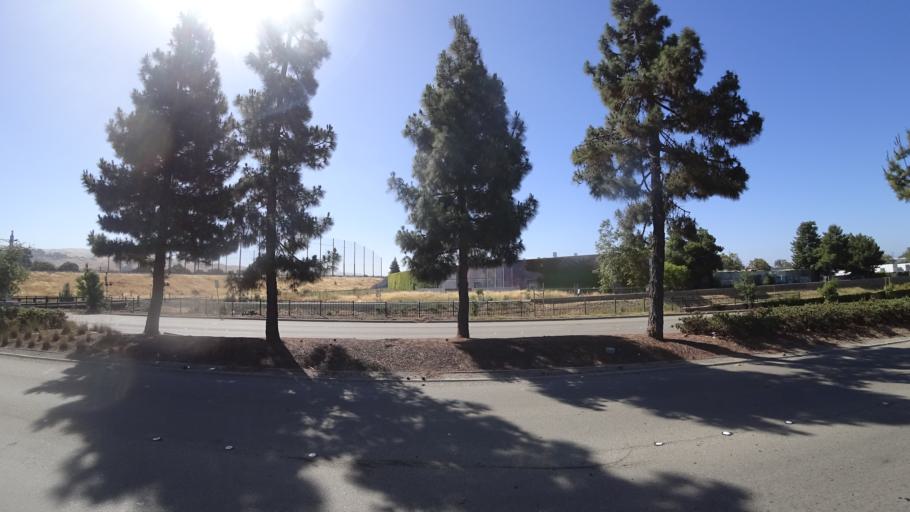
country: US
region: California
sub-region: Alameda County
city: Union City
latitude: 37.6248
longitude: -122.0532
